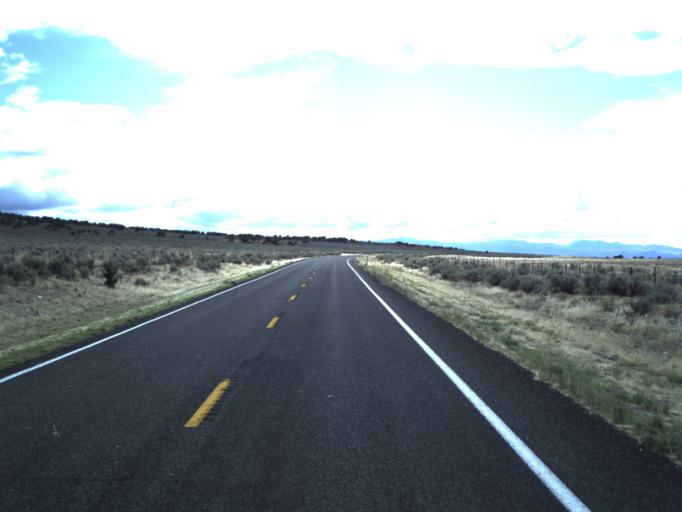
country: US
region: Utah
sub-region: Millard County
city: Fillmore
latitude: 39.0117
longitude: -112.4100
